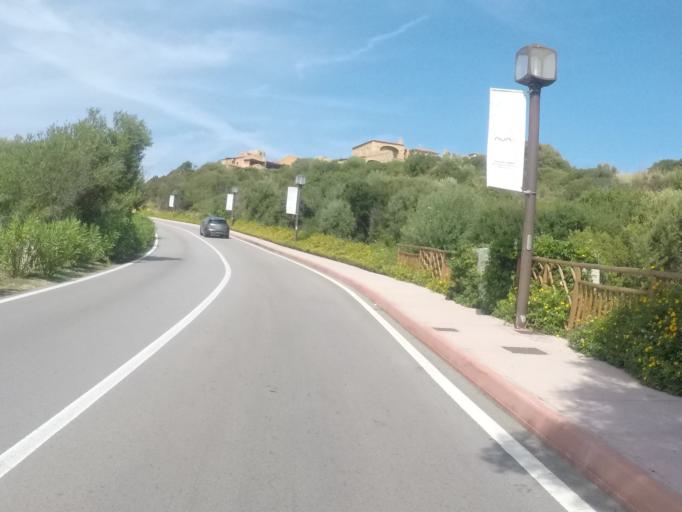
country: IT
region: Sardinia
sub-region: Provincia di Olbia-Tempio
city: Porto Cervo
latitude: 41.1246
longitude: 9.5367
